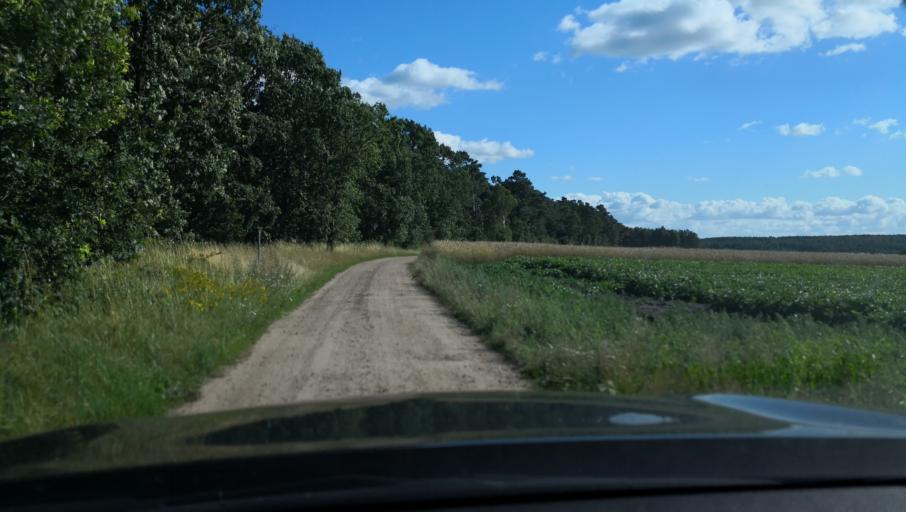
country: SE
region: Skane
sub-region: Kristianstads Kommun
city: Degeberga
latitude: 55.8042
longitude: 14.1970
